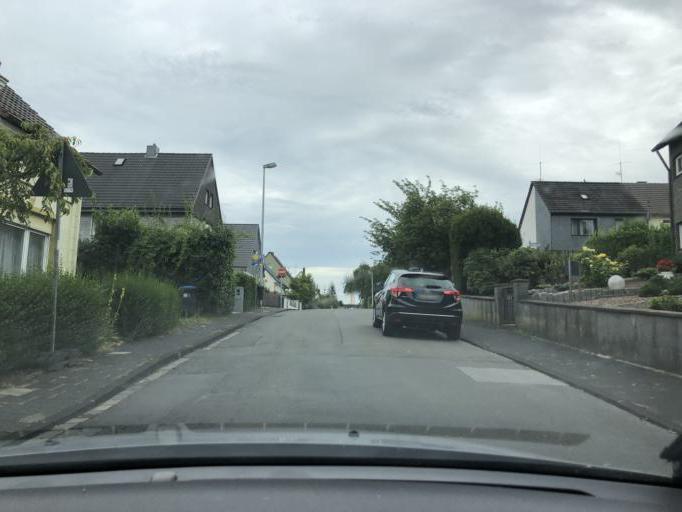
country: DE
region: North Rhine-Westphalia
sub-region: Regierungsbezirk Dusseldorf
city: Essen
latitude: 51.4347
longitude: 6.9512
